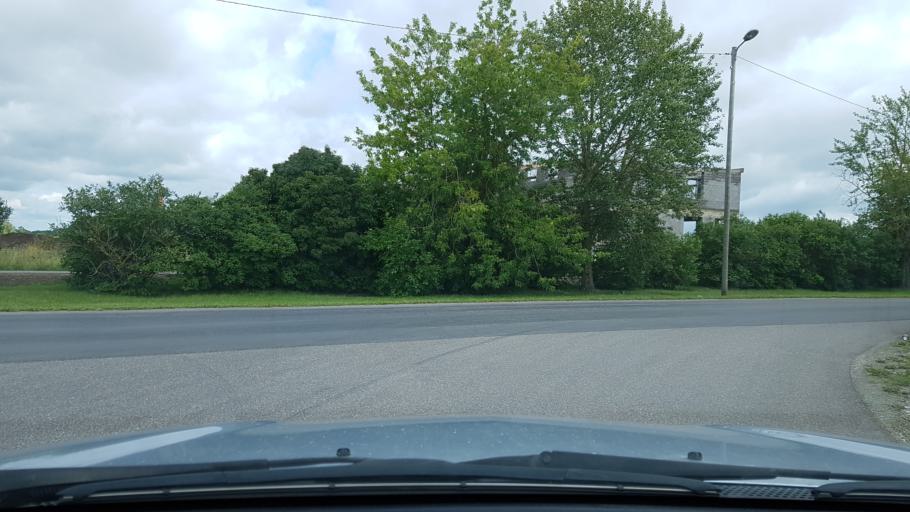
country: EE
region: Ida-Virumaa
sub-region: Narva linn
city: Narva
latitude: 59.3907
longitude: 28.1303
